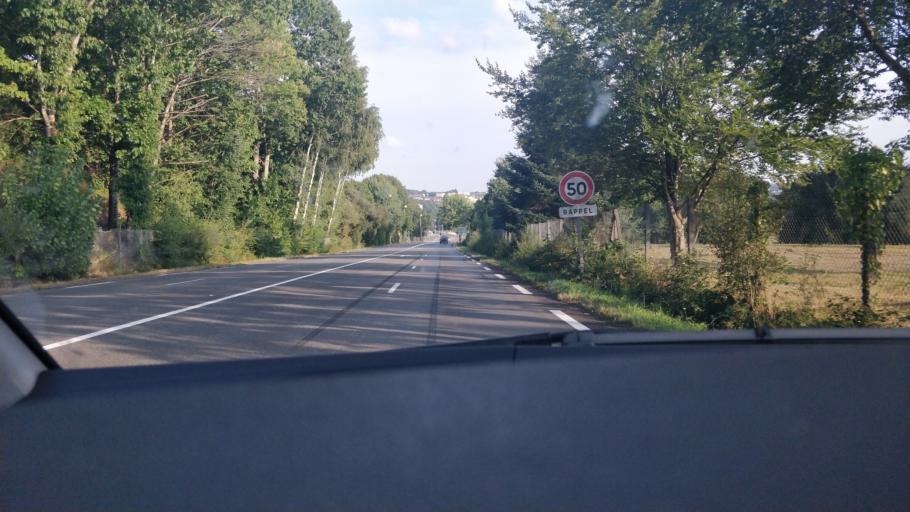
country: FR
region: Limousin
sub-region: Departement de la Haute-Vienne
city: Le Palais-sur-Vienne
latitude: 45.8540
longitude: 1.2952
